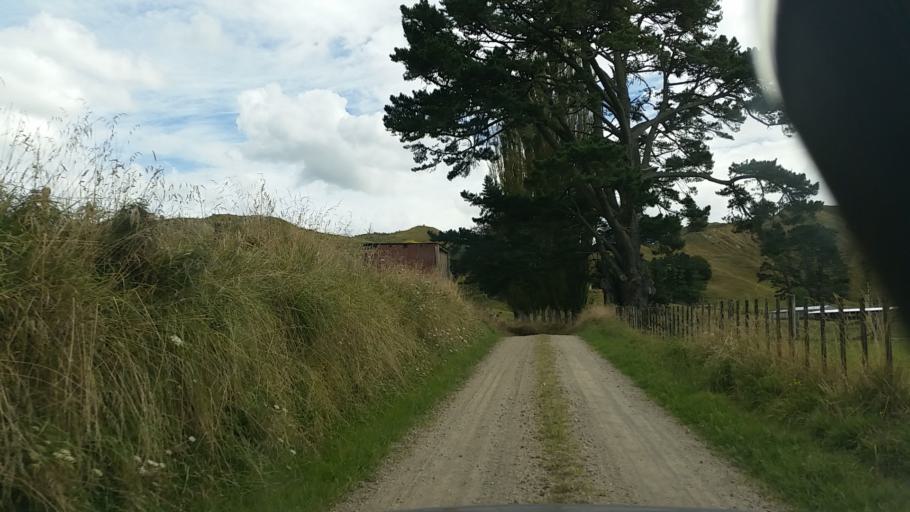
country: NZ
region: Taranaki
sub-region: South Taranaki District
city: Eltham
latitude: -39.2589
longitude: 174.5573
